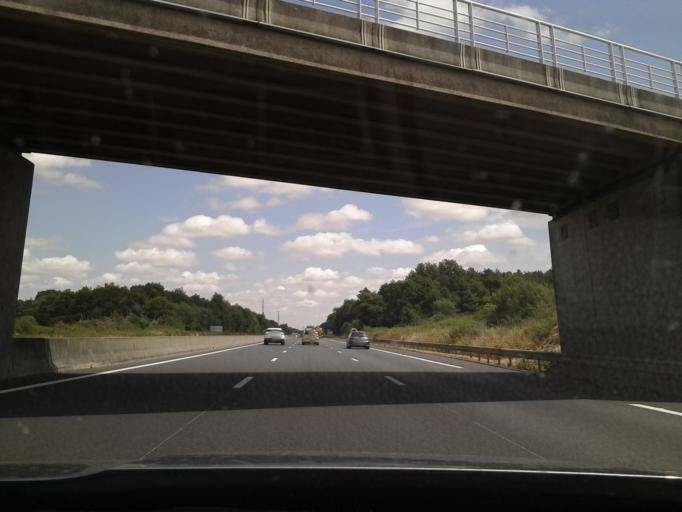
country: FR
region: Centre
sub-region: Departement d'Indre-et-Loire
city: Auzouer-en-Touraine
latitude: 47.5304
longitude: 0.9510
